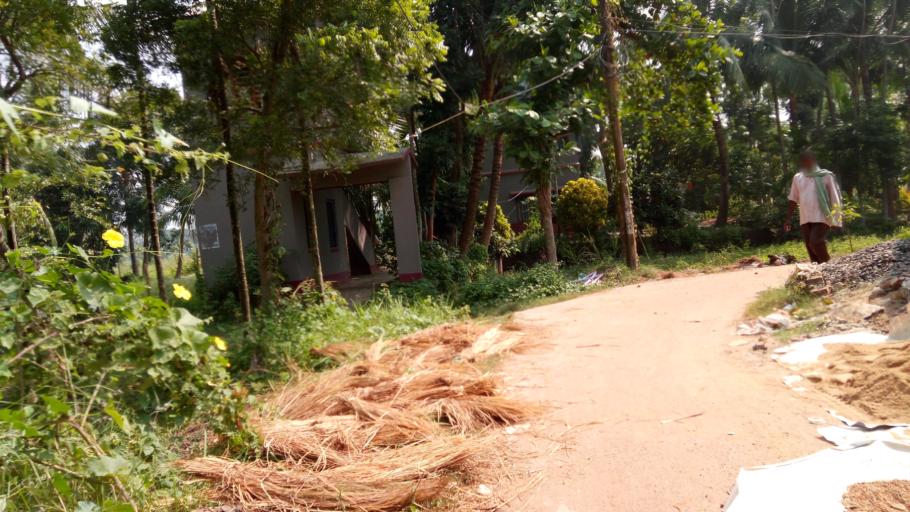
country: IN
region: West Bengal
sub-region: Purba Medinipur
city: Mahishadal
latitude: 22.1737
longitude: 87.9116
